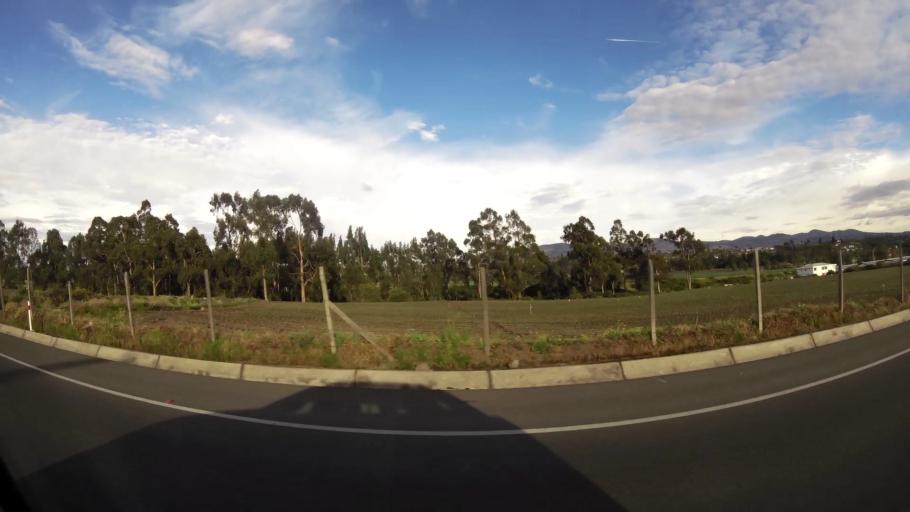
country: EC
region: Cotopaxi
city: Saquisili
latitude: -0.8426
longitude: -78.6193
